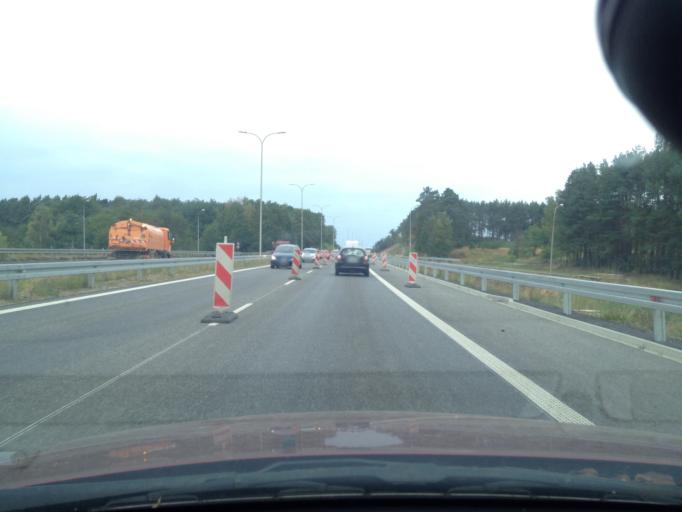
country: PL
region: Lubusz
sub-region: Zielona Gora
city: Zielona Gora
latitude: 51.9048
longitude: 15.5887
